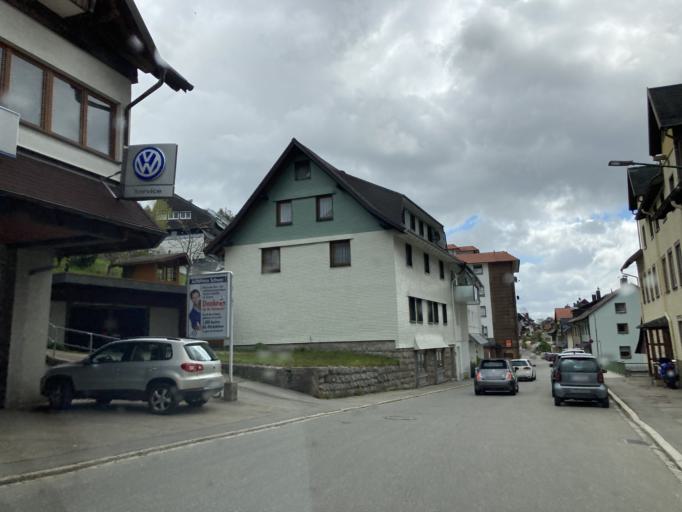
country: DE
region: Baden-Wuerttemberg
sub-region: Freiburg Region
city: Schonach im Schwarzwald
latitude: 48.1455
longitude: 8.1946
